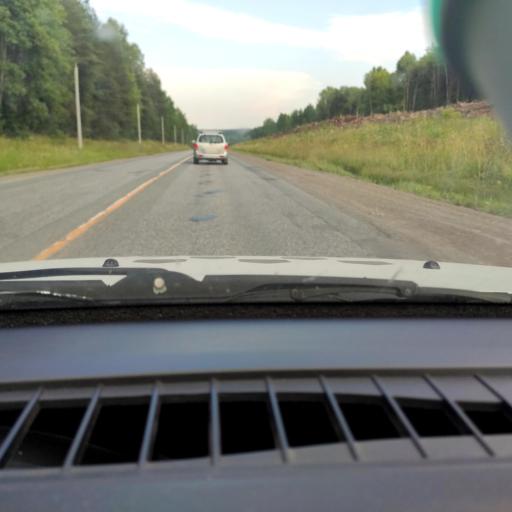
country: RU
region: Perm
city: Kukushtan
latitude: 57.5991
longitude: 56.5290
